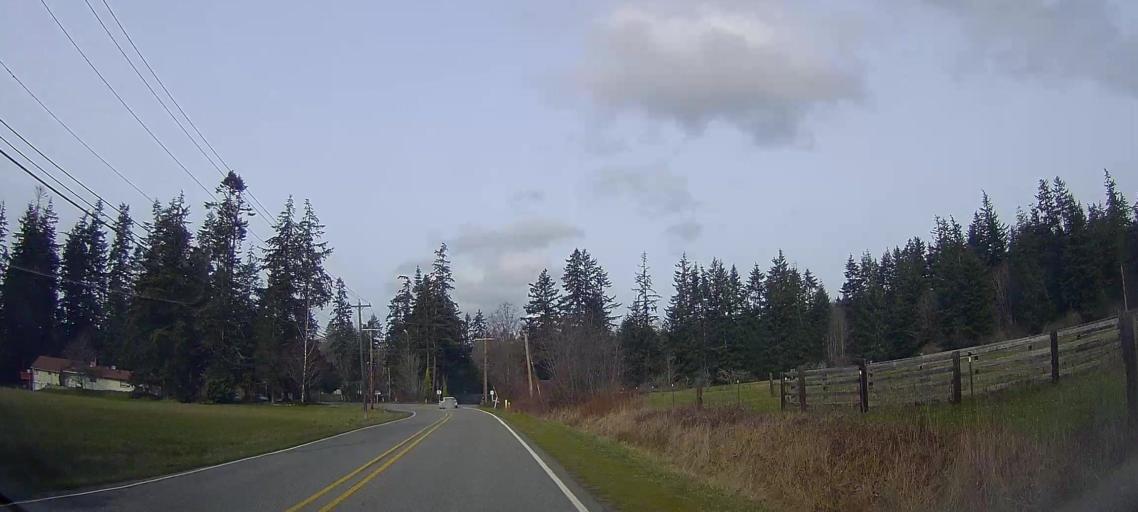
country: US
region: Washington
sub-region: Island County
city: Camano
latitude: 48.1596
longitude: -122.5166
